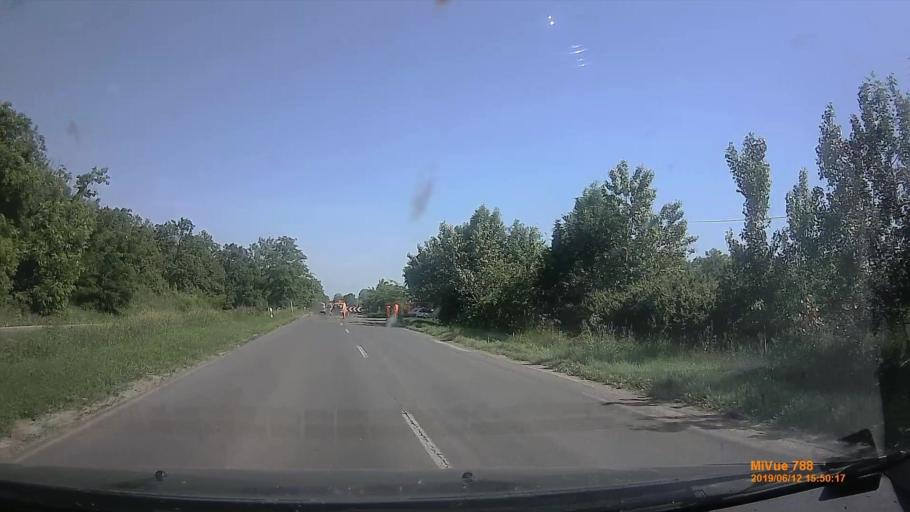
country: HU
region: Csongrad
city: Apatfalva
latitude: 46.1877
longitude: 20.5649
